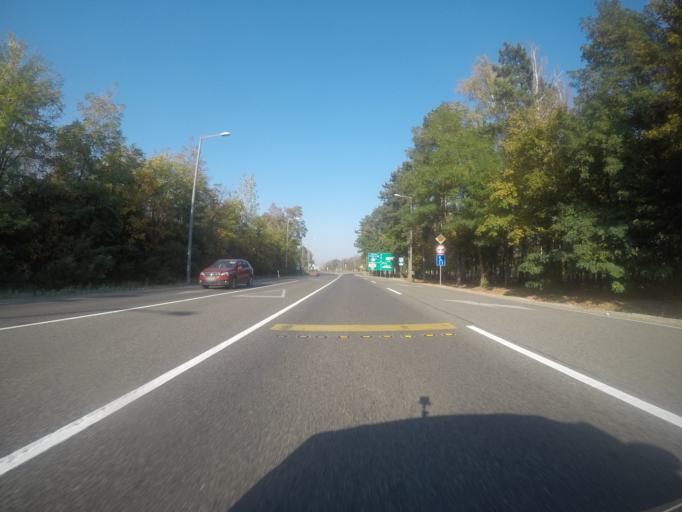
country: HU
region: Fejer
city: Racalmas
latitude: 46.9975
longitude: 18.9293
